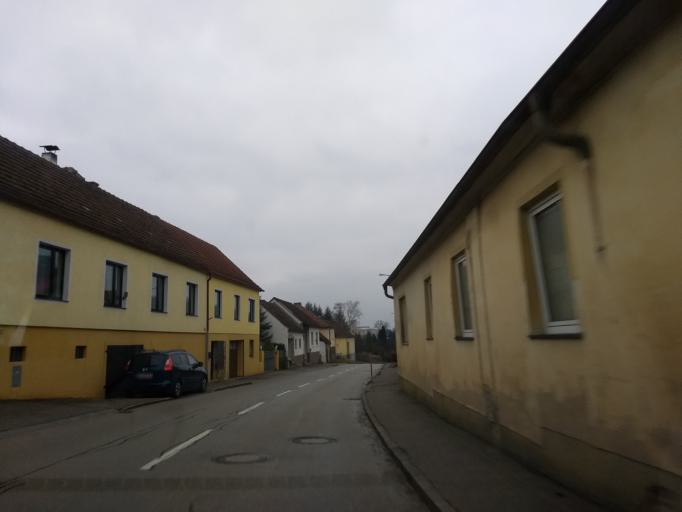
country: AT
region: Lower Austria
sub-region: Politischer Bezirk Tulln
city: Sieghartskirchen
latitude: 48.2306
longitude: 16.0216
